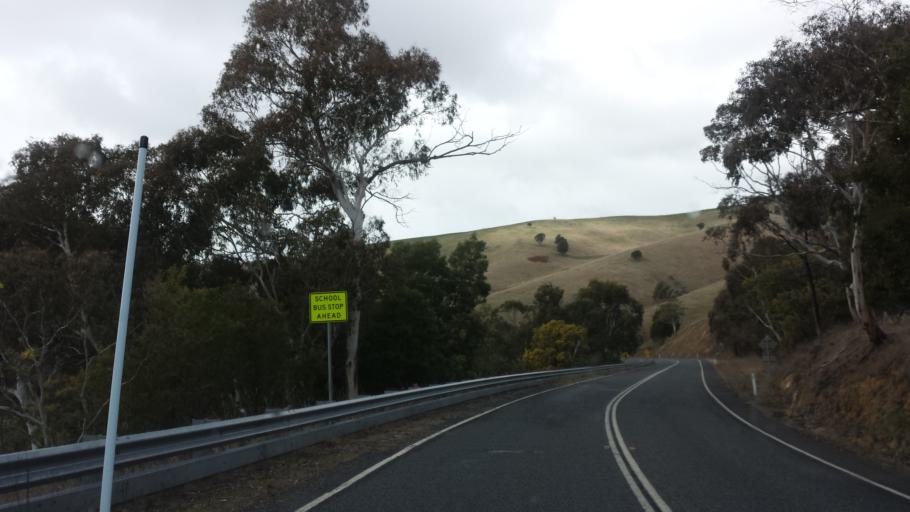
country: AU
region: Victoria
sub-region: Alpine
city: Mount Beauty
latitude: -37.1179
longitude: 147.5467
